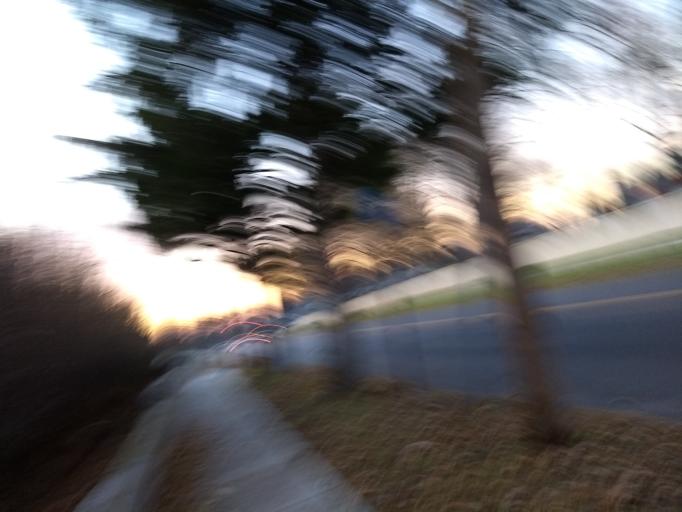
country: US
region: New York
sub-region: Onondaga County
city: Mattydale
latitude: 43.0743
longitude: -76.1518
